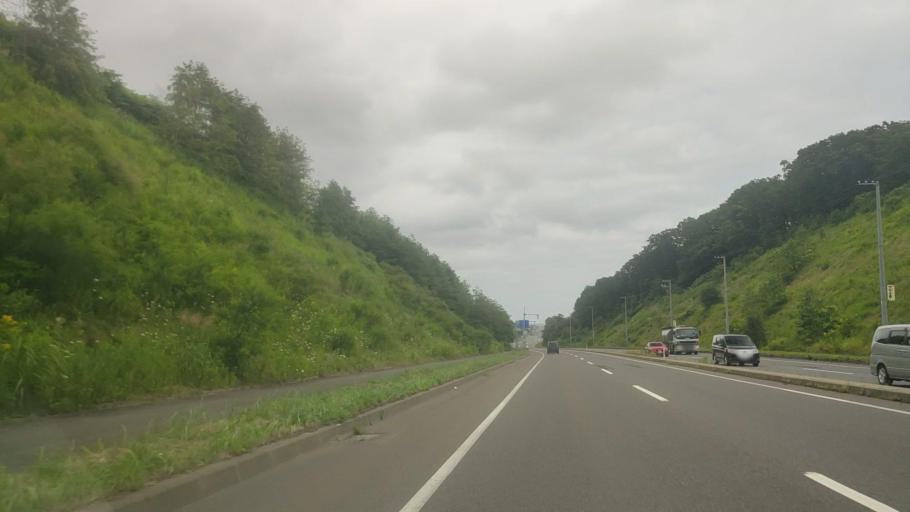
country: JP
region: Hokkaido
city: Shiraoi
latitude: 42.4573
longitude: 141.1951
